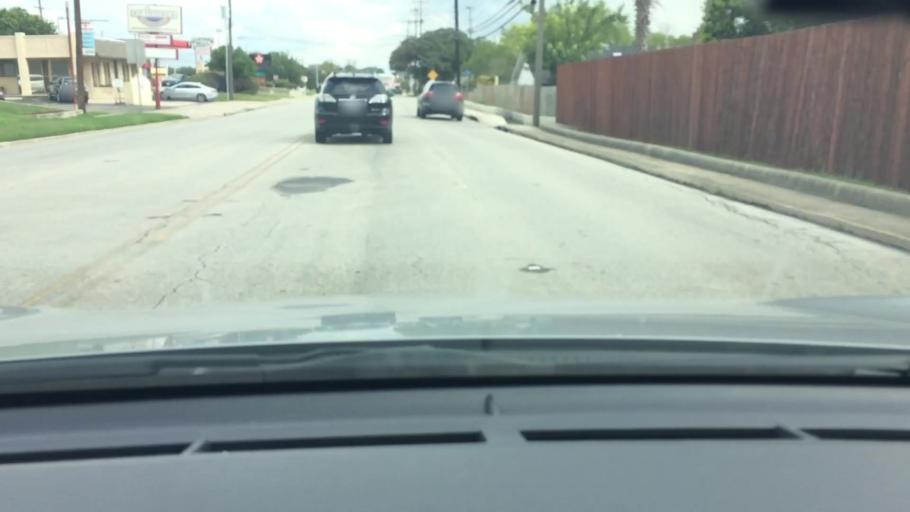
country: US
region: Texas
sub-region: Bexar County
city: Castle Hills
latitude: 29.5424
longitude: -98.5298
